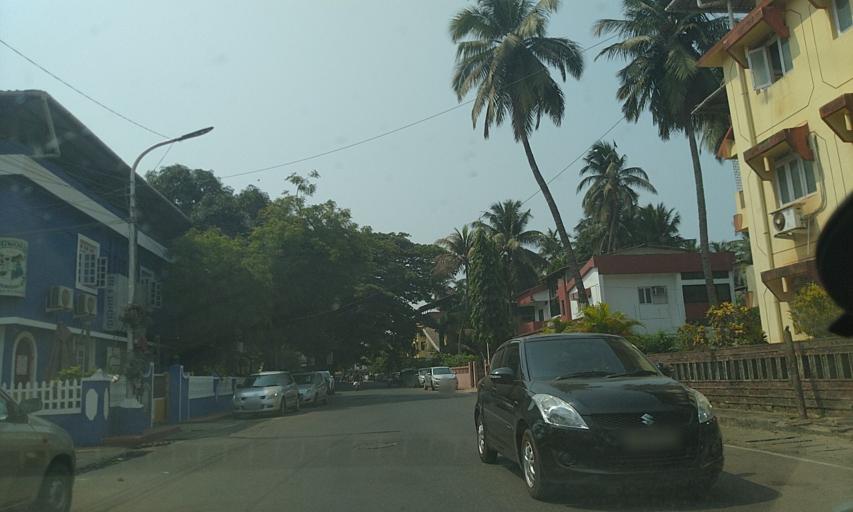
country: IN
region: Goa
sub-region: North Goa
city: Panaji
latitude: 15.4859
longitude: 73.8135
